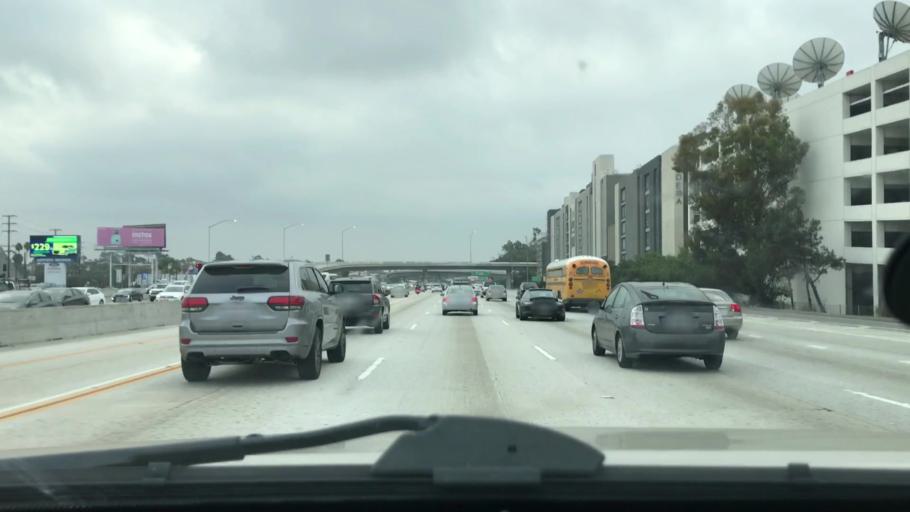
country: US
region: California
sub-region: Los Angeles County
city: Ladera Heights
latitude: 33.9768
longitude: -118.3887
